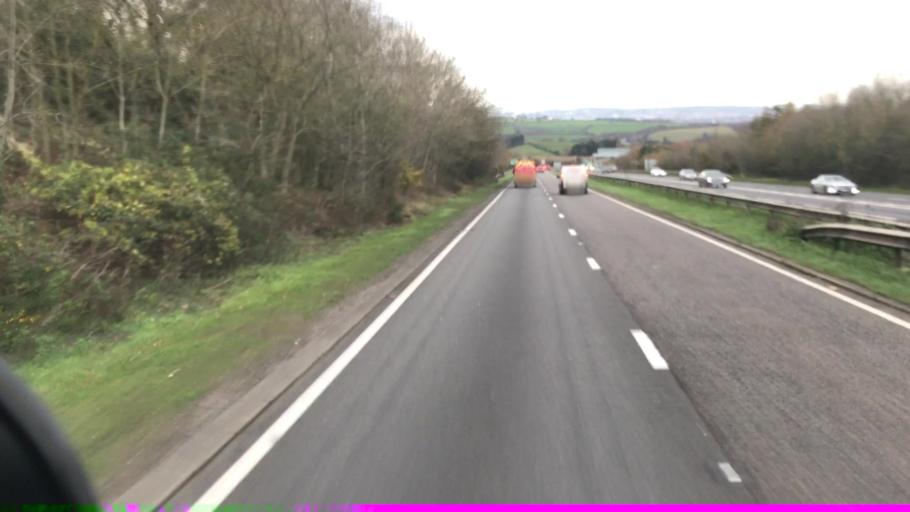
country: GB
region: England
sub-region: Devon
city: Exminster
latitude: 50.6515
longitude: -3.5415
